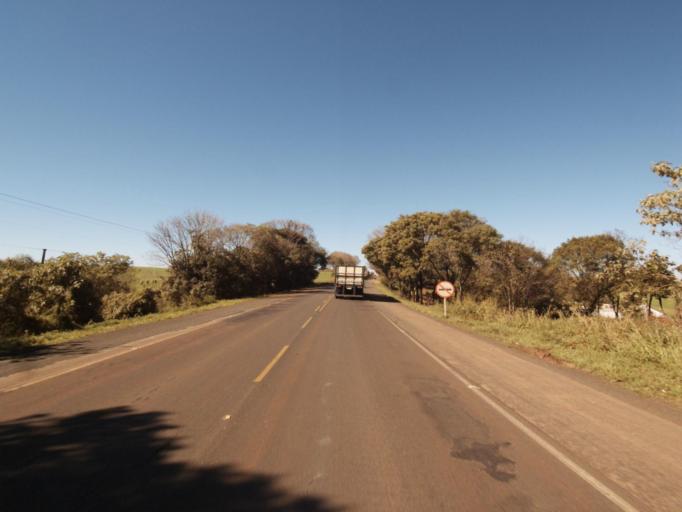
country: BR
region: Santa Catarina
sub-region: Chapeco
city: Chapeco
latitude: -26.8666
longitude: -52.9665
